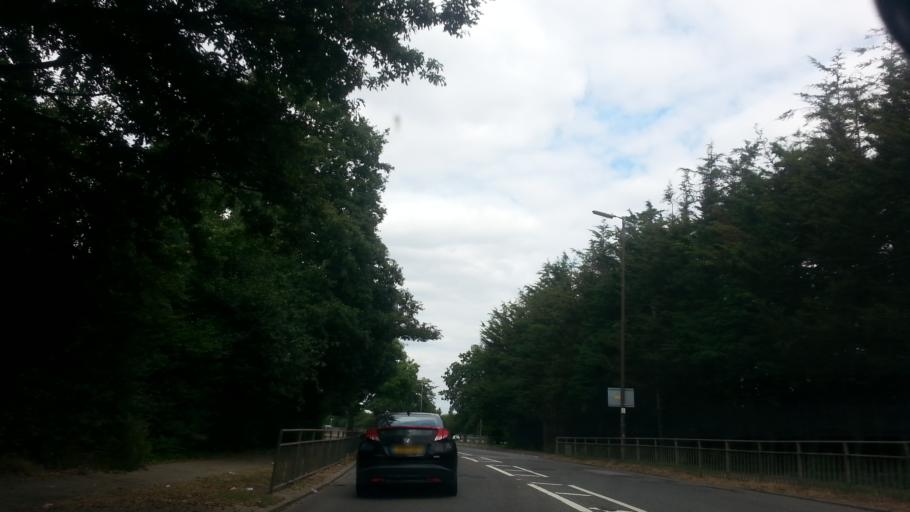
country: GB
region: England
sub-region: Essex
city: Chelmsford
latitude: 51.7211
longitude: 0.4699
